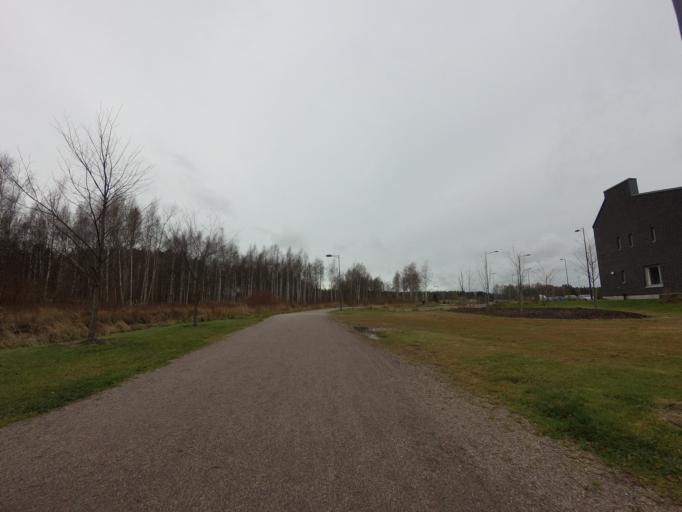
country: FI
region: Uusimaa
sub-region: Helsinki
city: Kauniainen
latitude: 60.1891
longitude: 24.7365
